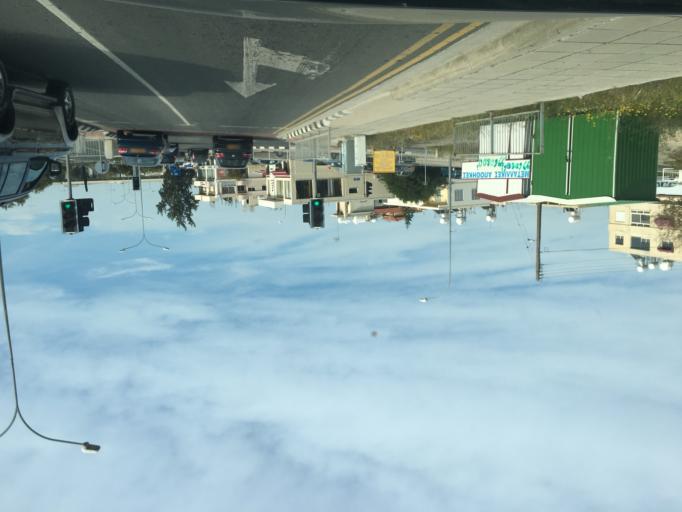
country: CY
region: Limassol
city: Pano Polemidia
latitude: 34.6969
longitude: 33.0118
